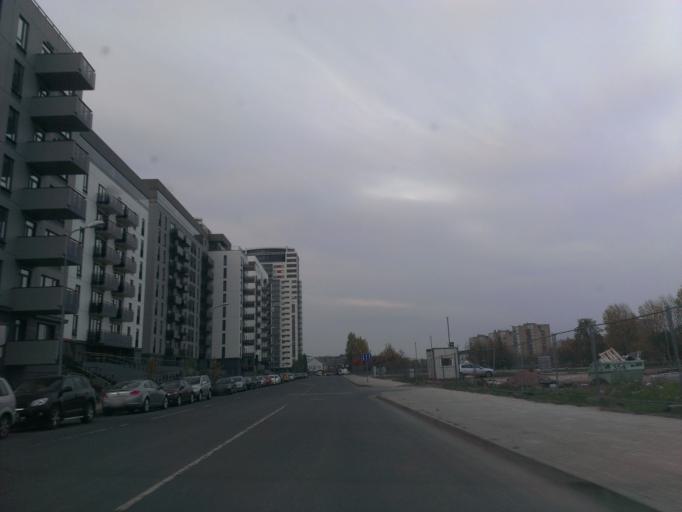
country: LV
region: Riga
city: Riga
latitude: 56.9695
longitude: 24.1244
